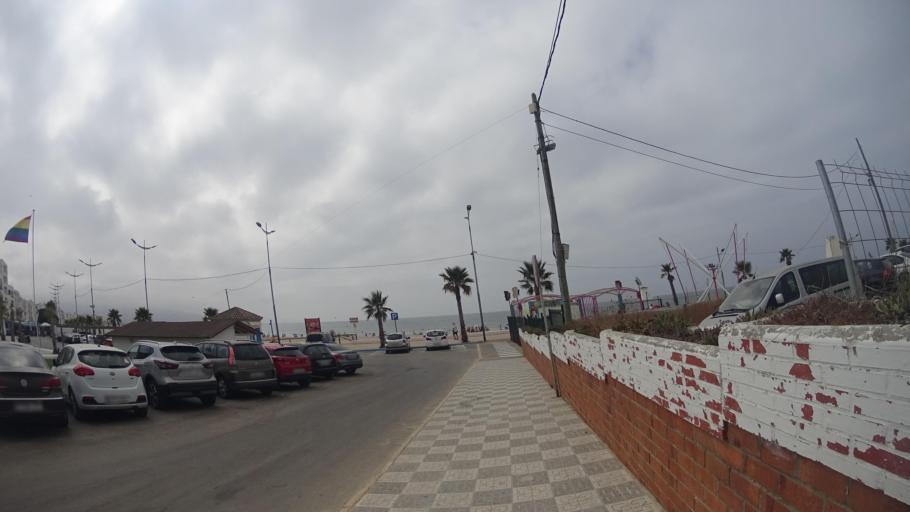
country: ES
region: Andalusia
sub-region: Provincia de Cadiz
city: Barbate de Franco
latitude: 36.1871
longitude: -5.9225
